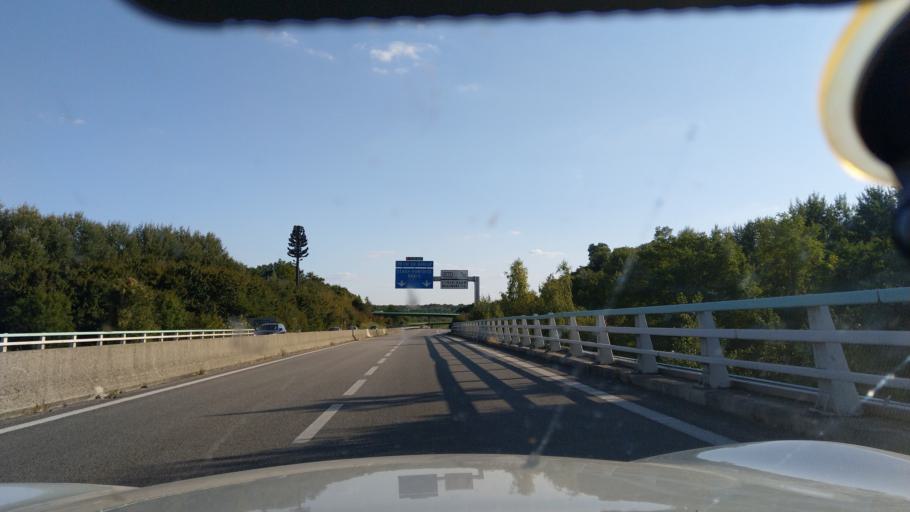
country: FR
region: Ile-de-France
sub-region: Departement du Val-d'Oise
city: Mours
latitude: 49.1314
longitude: 2.2536
